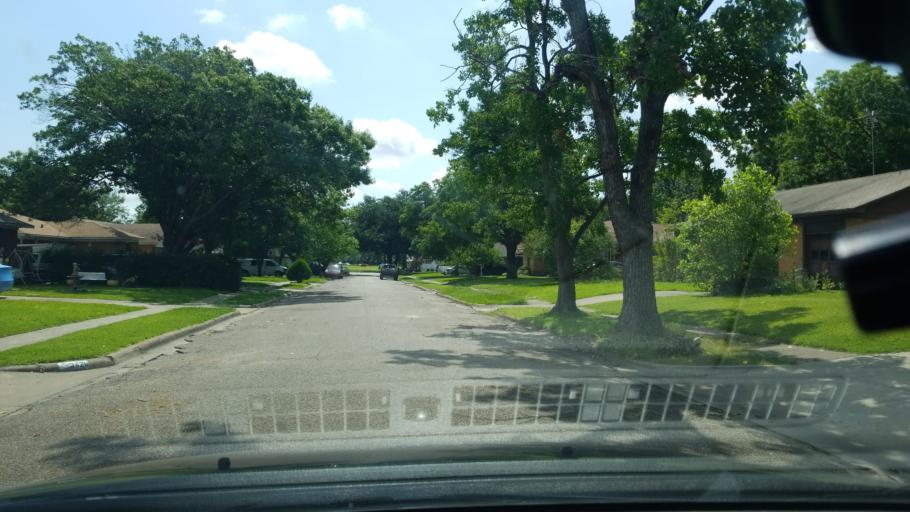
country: US
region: Texas
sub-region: Dallas County
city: Mesquite
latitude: 32.8156
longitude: -96.6512
